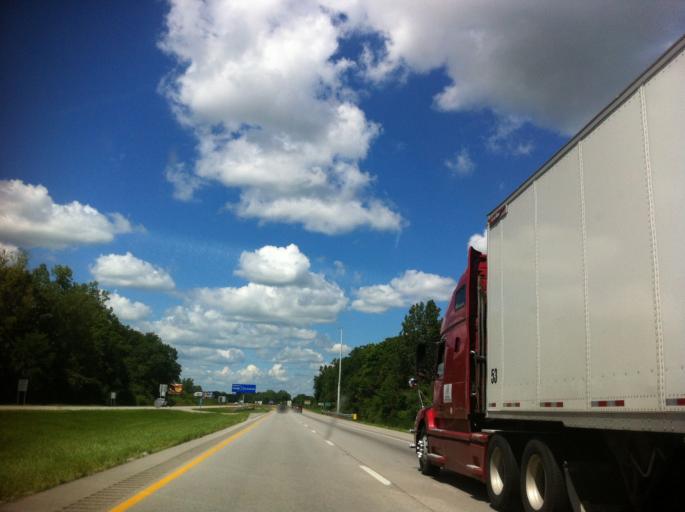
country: US
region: Ohio
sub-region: Lucas County
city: Sylvania
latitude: 41.7243
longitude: -83.6886
